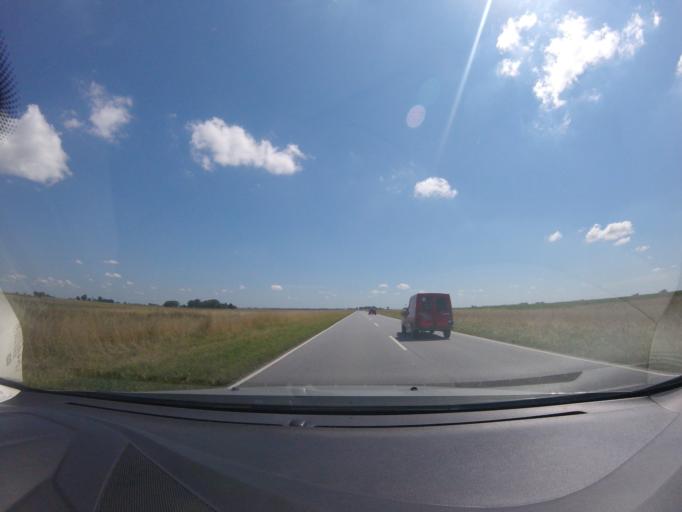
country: AR
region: Buenos Aires
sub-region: Partido de Rauch
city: Rauch
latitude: -36.9965
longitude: -59.0021
